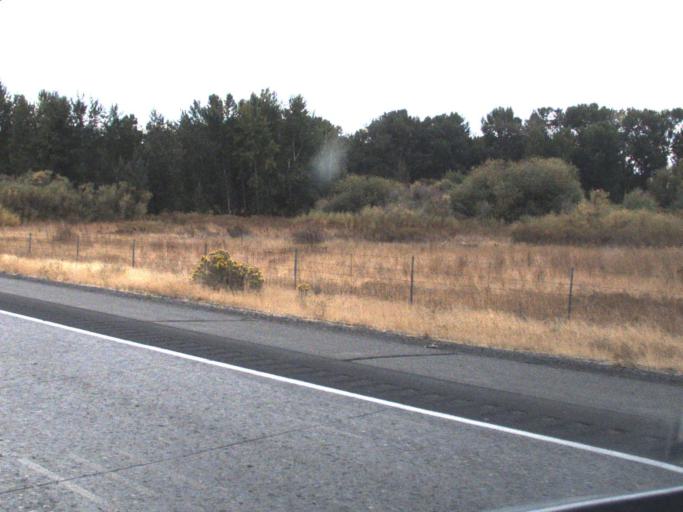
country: US
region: Washington
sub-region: Yakima County
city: Wapato
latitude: 46.4777
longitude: -120.4043
